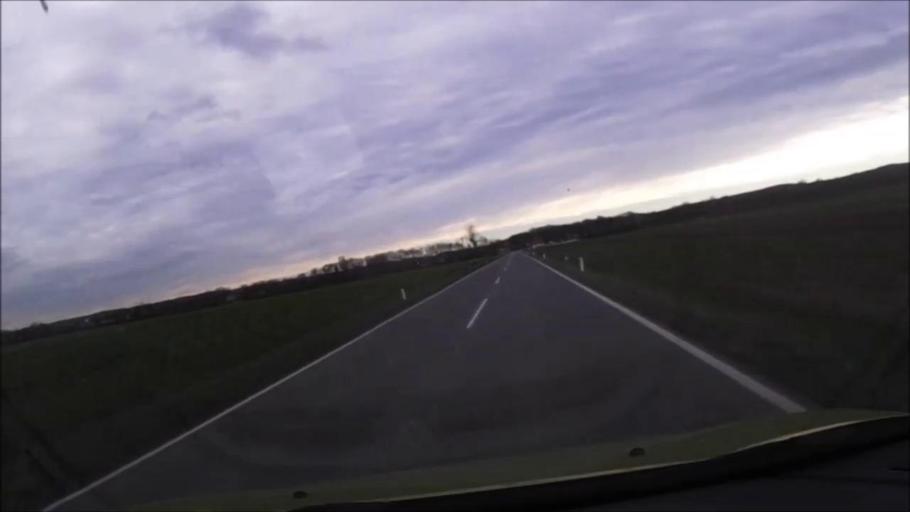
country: AT
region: Burgenland
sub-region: Eisenstadt-Umgebung
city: Leithaprodersdorf
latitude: 47.9457
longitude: 16.4606
